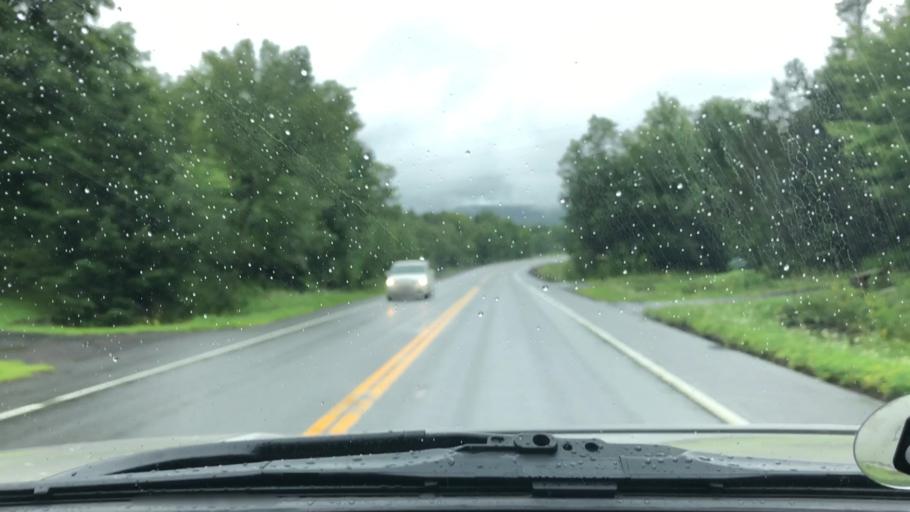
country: US
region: New York
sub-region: Greene County
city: Cairo
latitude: 42.3038
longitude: -74.2137
